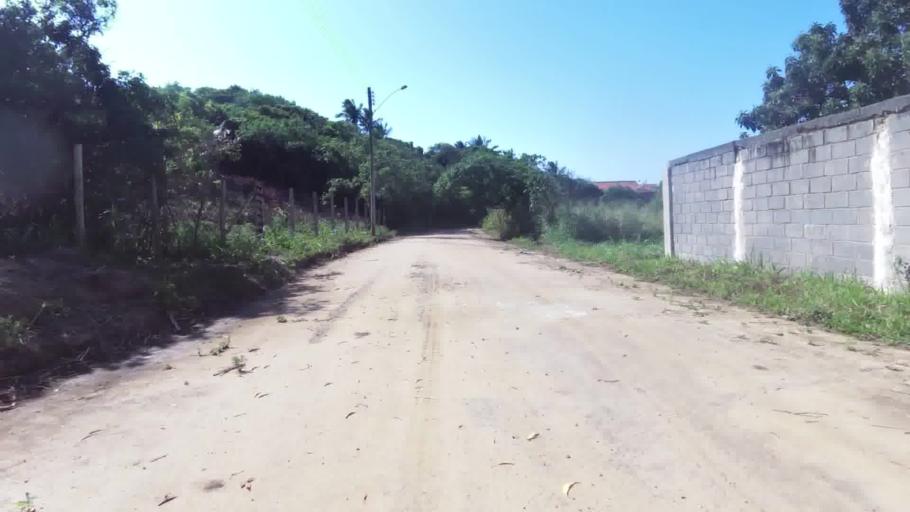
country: BR
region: Espirito Santo
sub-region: Piuma
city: Piuma
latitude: -20.8216
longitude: -40.6166
